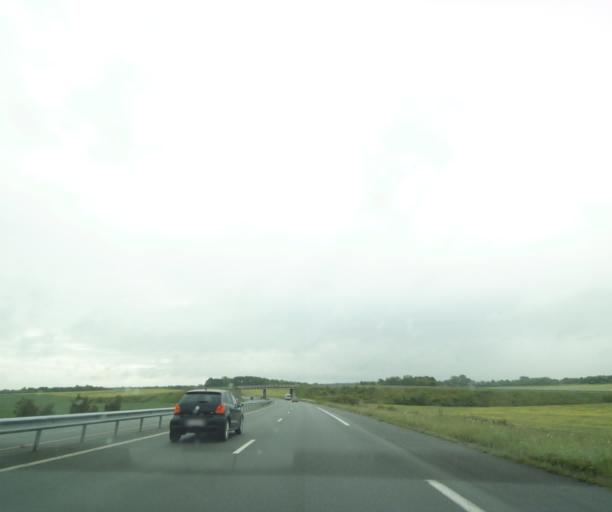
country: FR
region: Poitou-Charentes
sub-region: Departement de la Charente-Maritime
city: Nieul-les-Saintes
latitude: 45.6975
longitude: -0.7422
